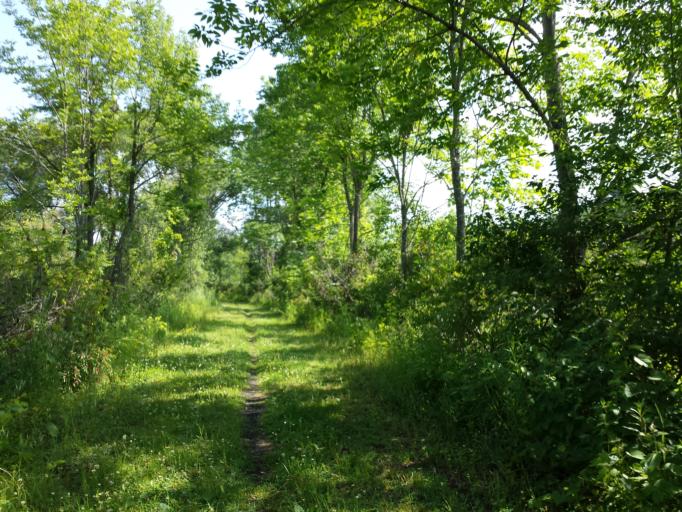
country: US
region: Vermont
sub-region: Rutland County
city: Poultney
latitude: 43.5035
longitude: -73.2390
